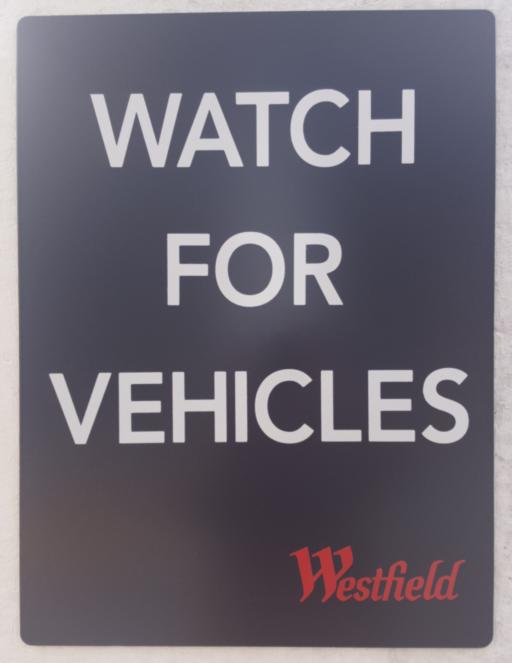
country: US
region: Illinois
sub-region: Cook County
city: Wilmette
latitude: 42.0595
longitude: -87.7506
